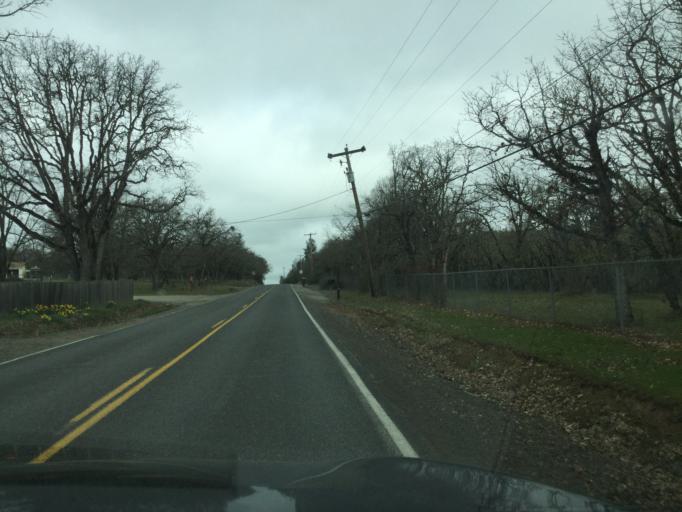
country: US
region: Oregon
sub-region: Jackson County
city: Central Point
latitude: 42.3890
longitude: -122.9851
